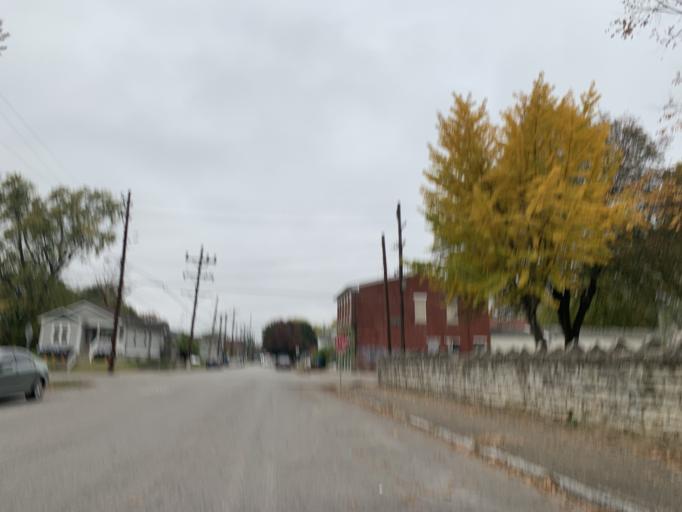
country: US
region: Kentucky
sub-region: Jefferson County
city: Louisville
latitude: 38.2608
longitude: -85.7824
